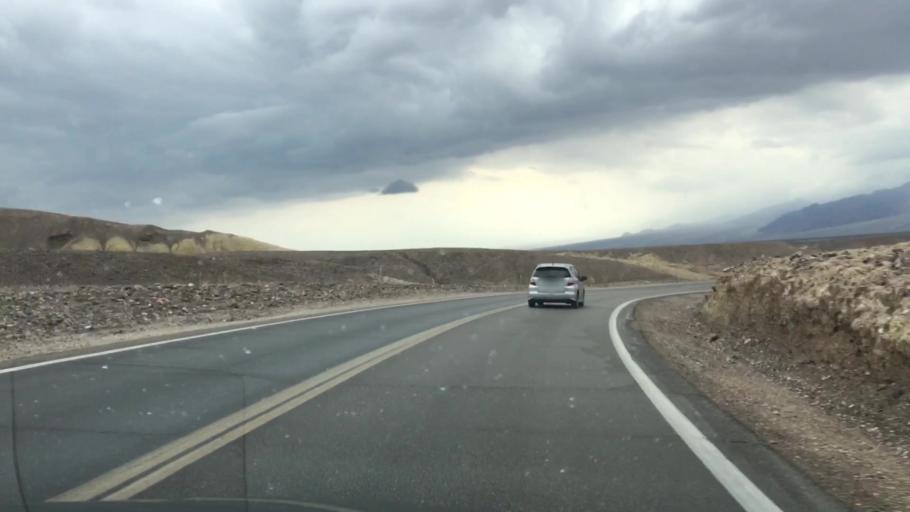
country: US
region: Nevada
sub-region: Nye County
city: Beatty
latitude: 36.4868
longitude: -116.8686
